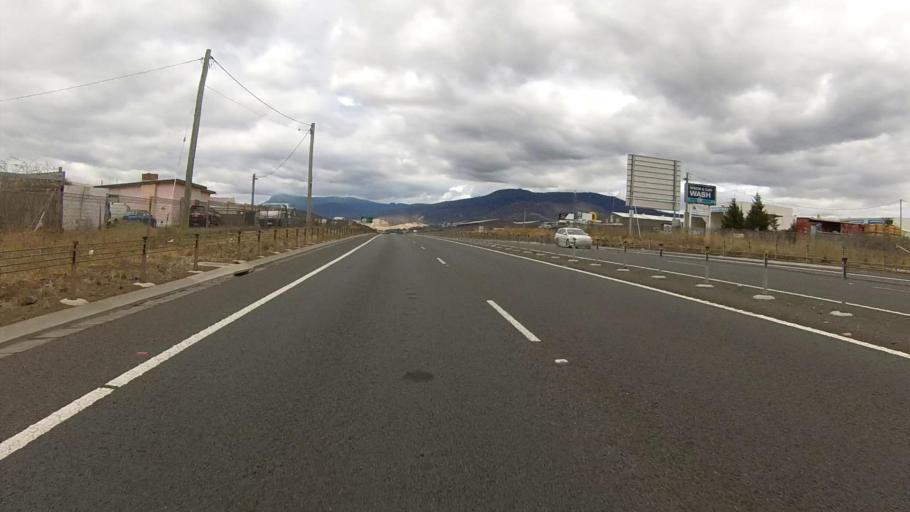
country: AU
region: Tasmania
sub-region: Brighton
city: Bridgewater
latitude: -42.7191
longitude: 147.2382
